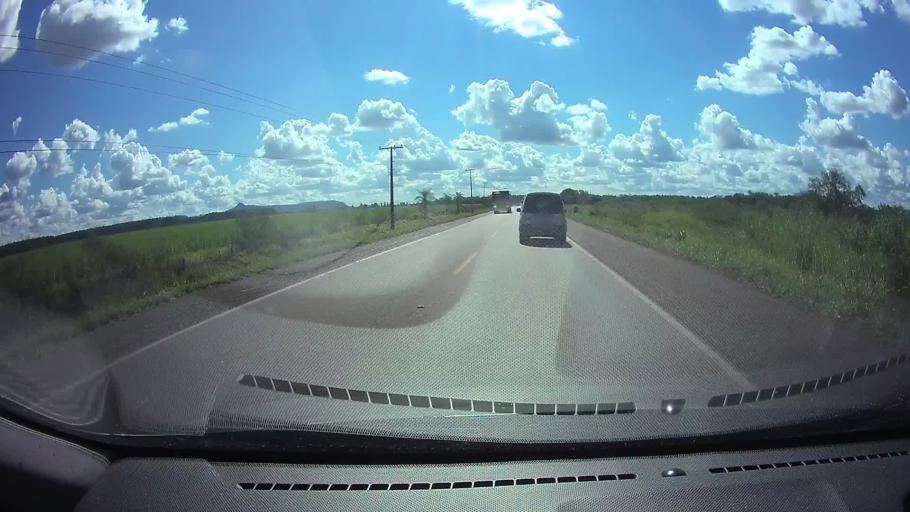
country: PY
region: Guaira
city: Coronel Martinez
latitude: -25.7626
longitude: -56.6887
